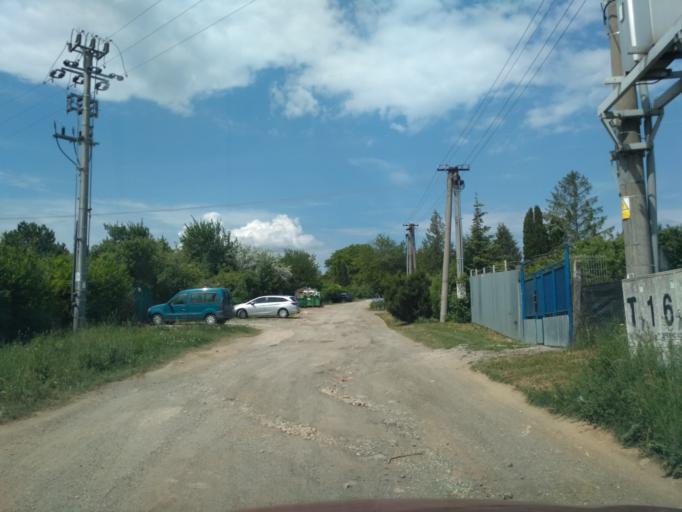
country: SK
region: Kosicky
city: Kosice
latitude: 48.7278
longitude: 21.2271
